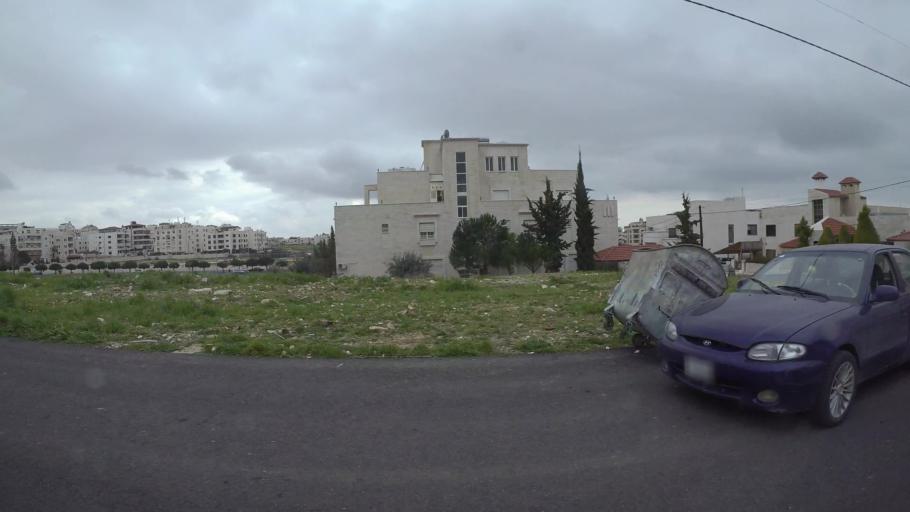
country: JO
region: Amman
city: Al Jubayhah
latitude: 31.9904
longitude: 35.8422
